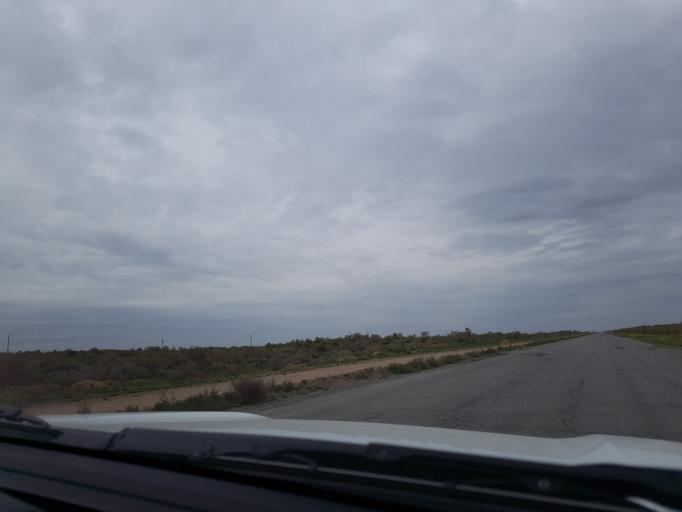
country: TM
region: Mary
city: Bayramaly
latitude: 37.8153
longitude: 62.5722
